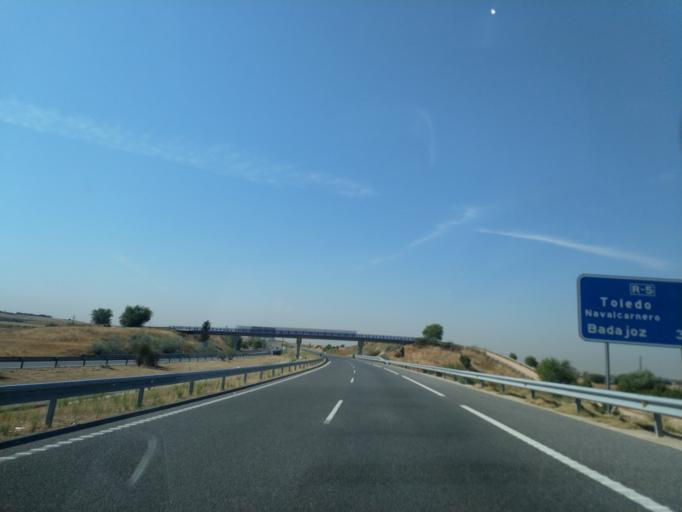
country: ES
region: Madrid
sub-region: Provincia de Madrid
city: Mostoles
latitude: 40.3034
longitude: -3.8476
